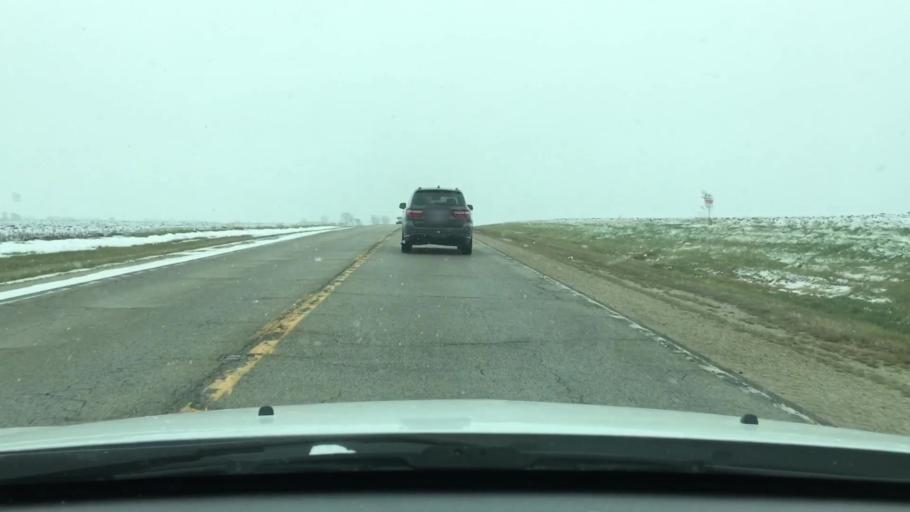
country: US
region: Illinois
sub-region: DeKalb County
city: Malta
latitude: 41.9353
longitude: -88.9491
